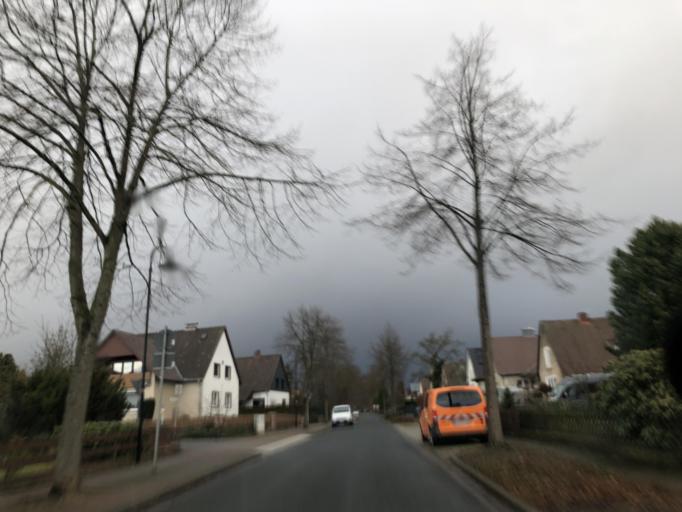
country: DE
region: Lower Saxony
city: Bad Fallingbostel
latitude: 52.8802
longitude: 9.7077
